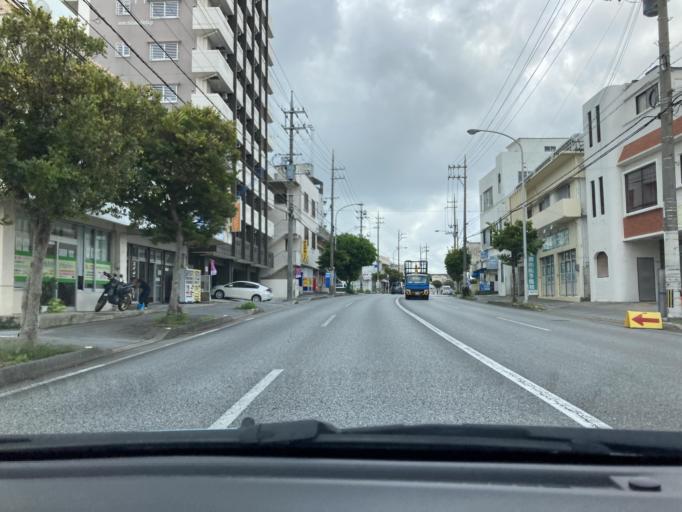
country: JP
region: Okinawa
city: Okinawa
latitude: 26.3411
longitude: 127.8181
